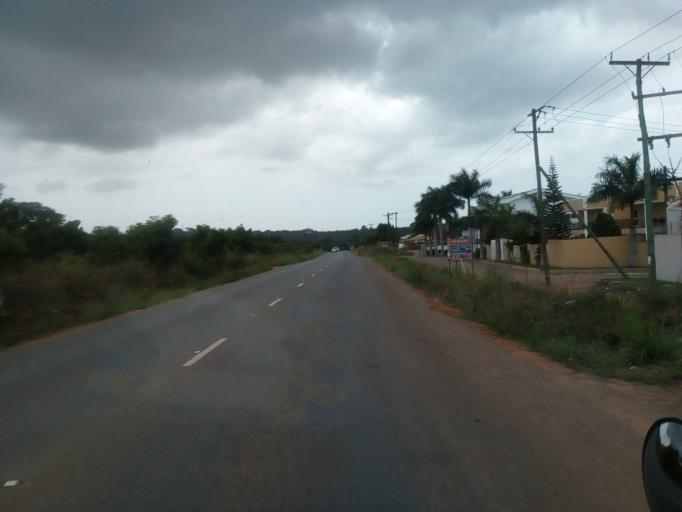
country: GH
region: Greater Accra
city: Dome
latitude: 5.6504
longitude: -0.2052
